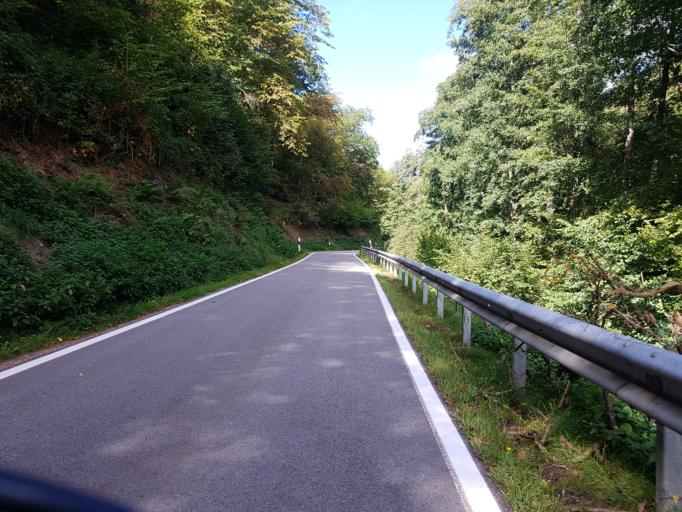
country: DE
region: Rheinland-Pfalz
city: Perscheid
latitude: 50.0598
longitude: 7.7231
